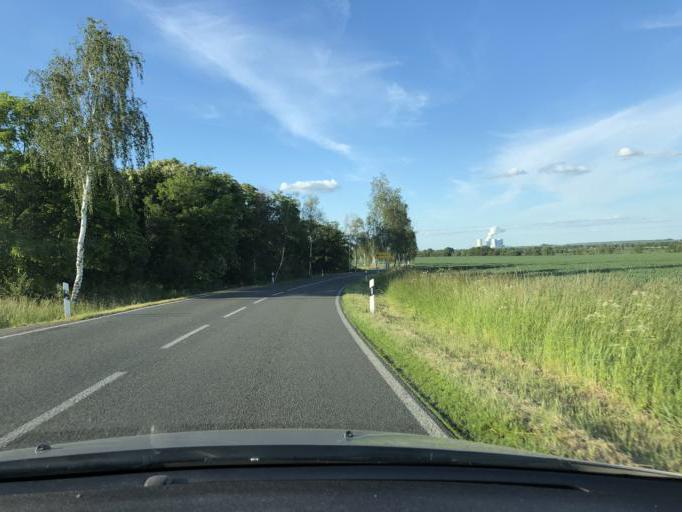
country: DE
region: Saxony
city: Groitzsch
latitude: 51.1234
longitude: 12.2861
